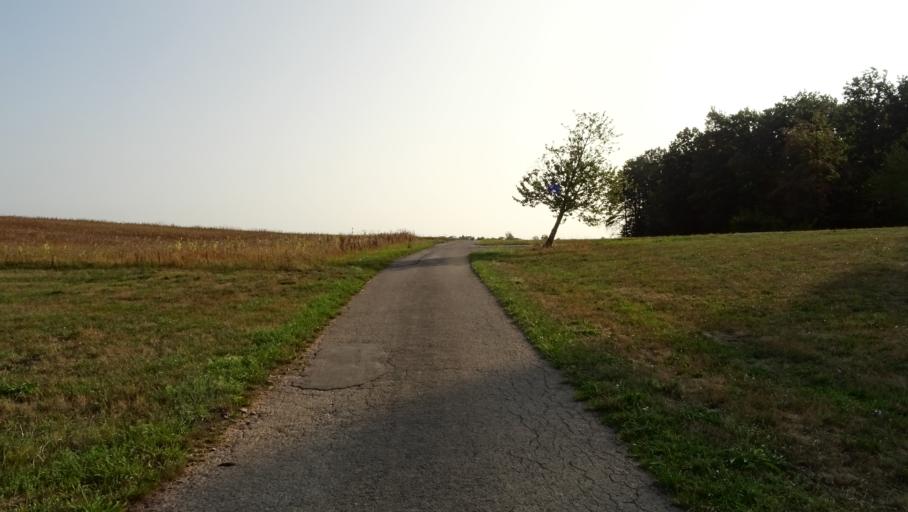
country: DE
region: Baden-Wuerttemberg
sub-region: Karlsruhe Region
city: Fahrenbach
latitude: 49.4232
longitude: 9.1383
